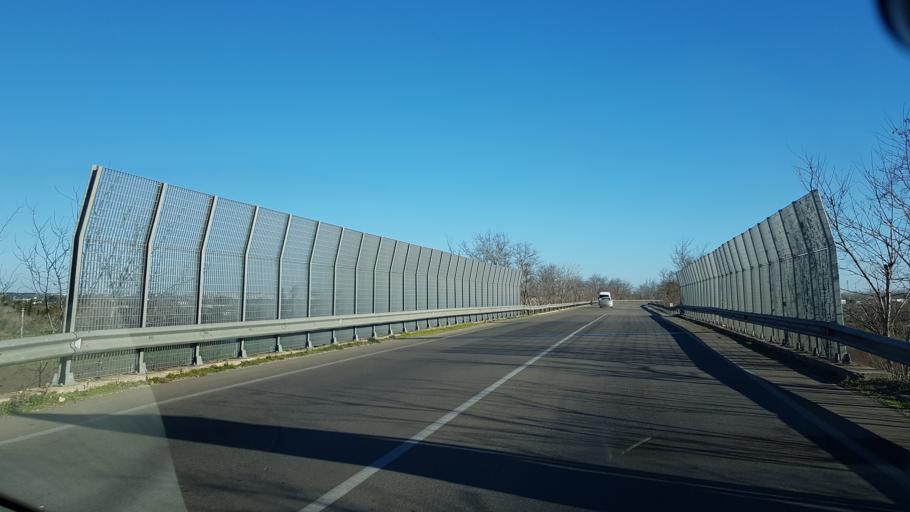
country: IT
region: Apulia
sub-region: Provincia di Lecce
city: Taviano
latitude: 39.9955
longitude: 18.0934
